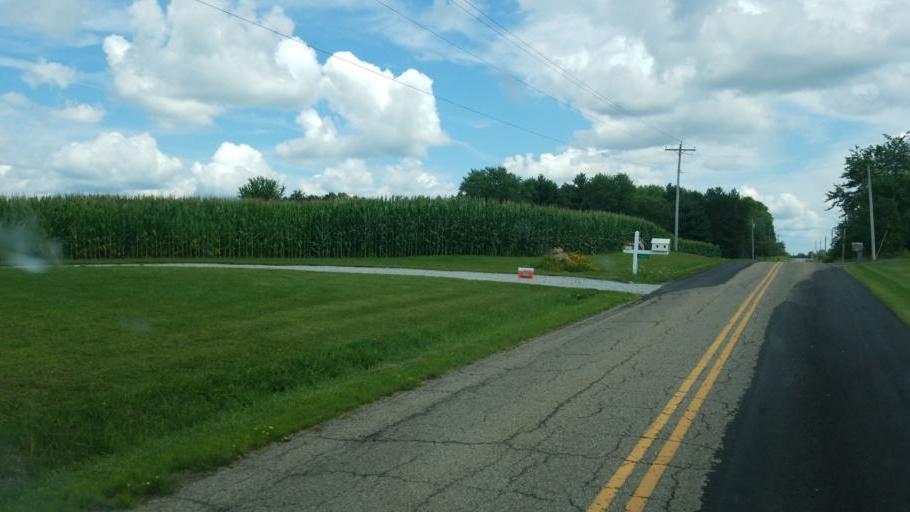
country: US
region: Ohio
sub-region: Knox County
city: Centerburg
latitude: 40.3743
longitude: -82.6115
